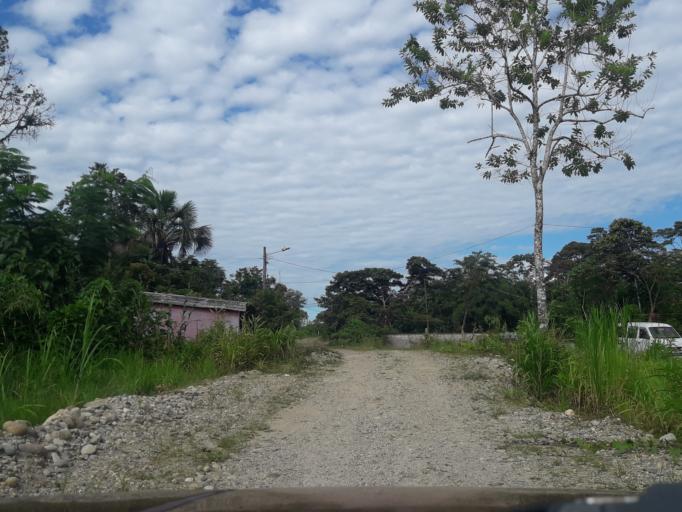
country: EC
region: Napo
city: Tena
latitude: -0.9812
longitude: -77.8191
